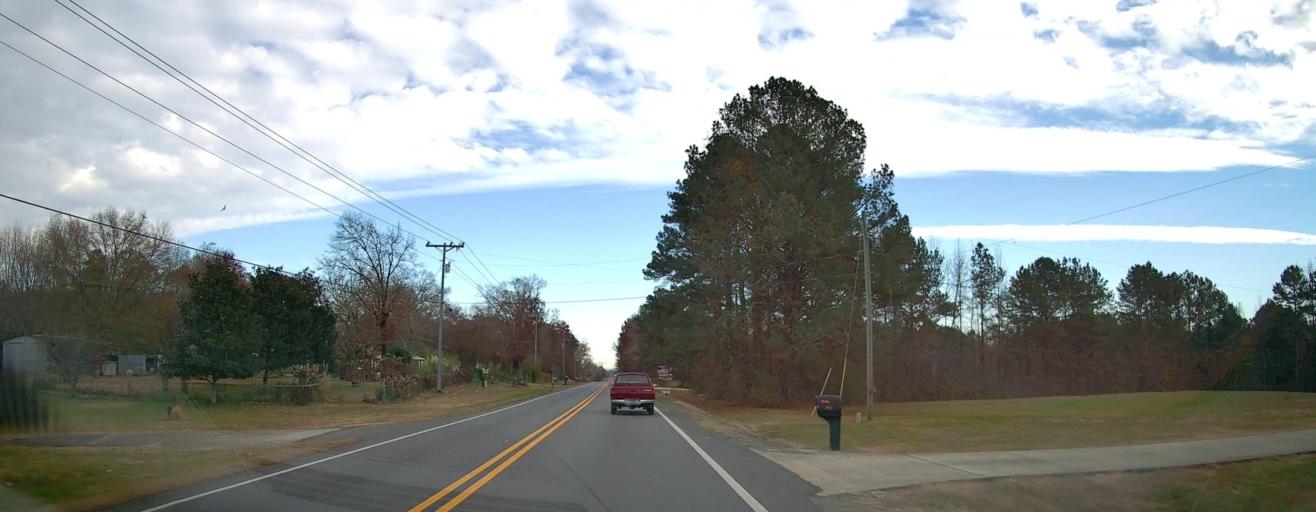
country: US
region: Alabama
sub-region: Morgan County
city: Priceville
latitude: 34.4878
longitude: -86.8353
